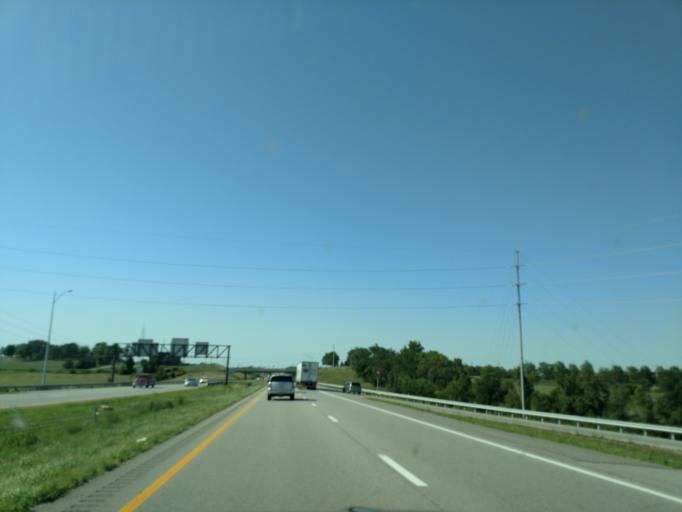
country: US
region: Missouri
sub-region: Buchanan County
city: Saint Joseph
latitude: 39.7513
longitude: -94.7897
